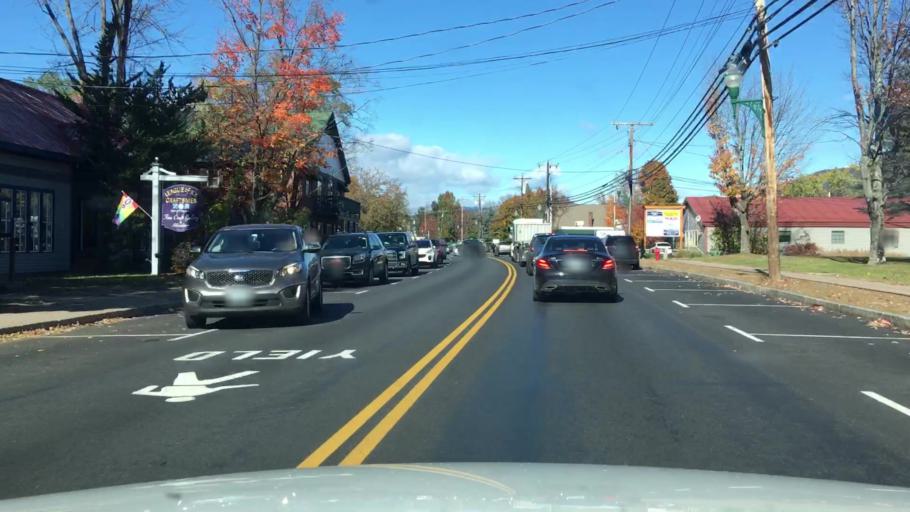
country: US
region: New Hampshire
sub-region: Carroll County
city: North Conway
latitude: 44.0486
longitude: -71.1247
